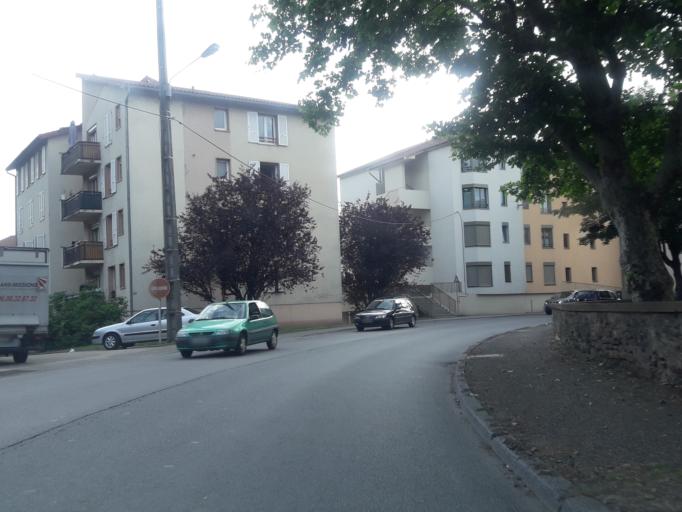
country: FR
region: Rhone-Alpes
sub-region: Departement du Rhone
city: Saint-Germain-Nuelles
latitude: 45.8349
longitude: 4.6201
